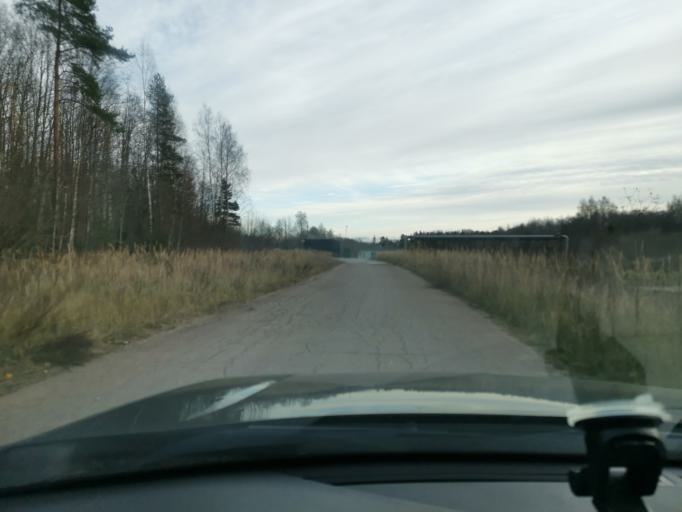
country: EE
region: Ida-Virumaa
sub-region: Sillamaee linn
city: Sillamae
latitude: 59.2613
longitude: 27.9078
